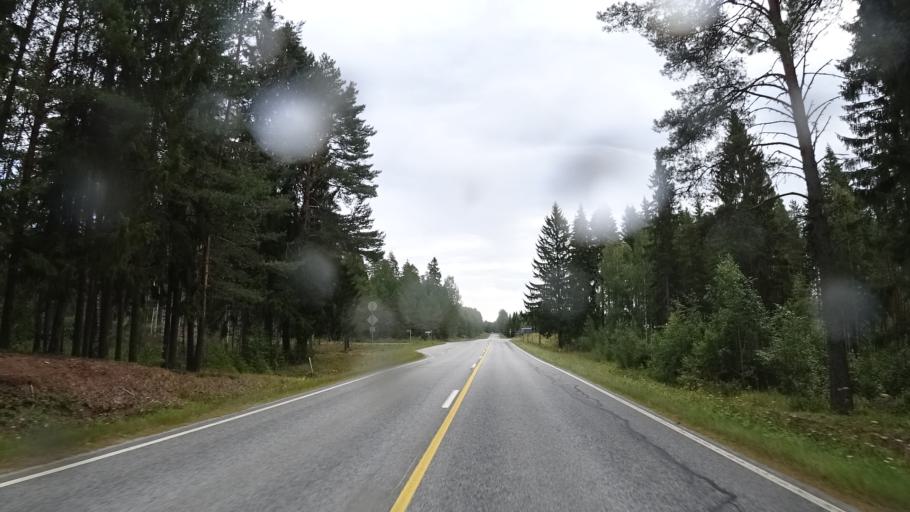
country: FI
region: North Karelia
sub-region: Keski-Karjala
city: Kesaelahti
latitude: 62.1104
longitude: 29.7373
